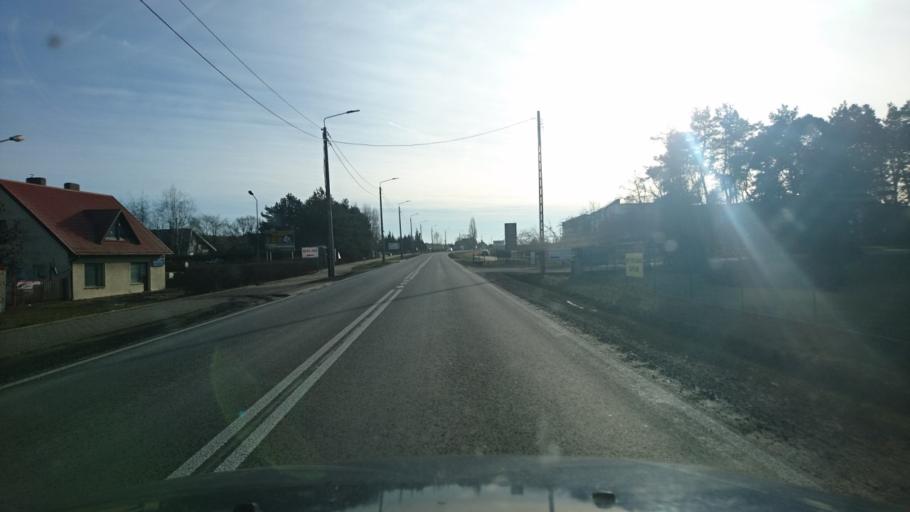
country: PL
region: Greater Poland Voivodeship
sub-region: Powiat ostrzeszowski
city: Ostrzeszow
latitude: 51.4441
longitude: 17.9123
